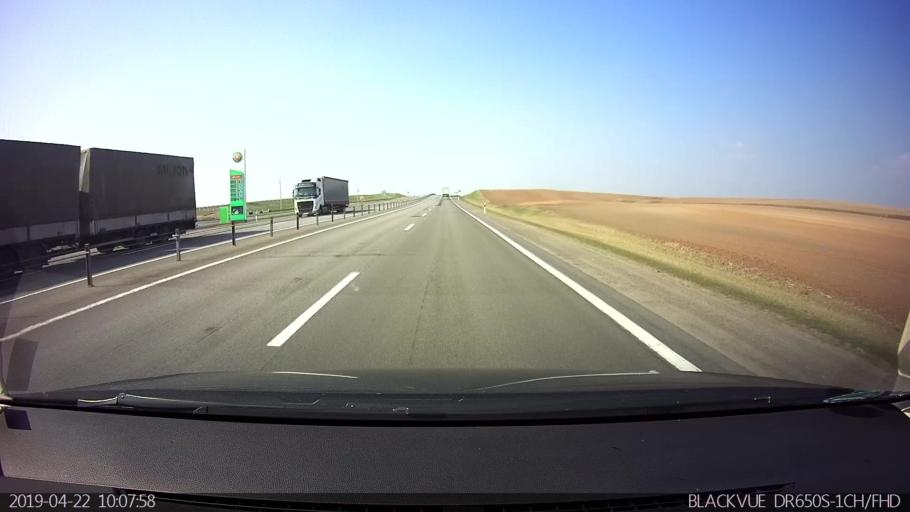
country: BY
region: Vitebsk
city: Horad Orsha
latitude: 54.6256
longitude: 30.4522
